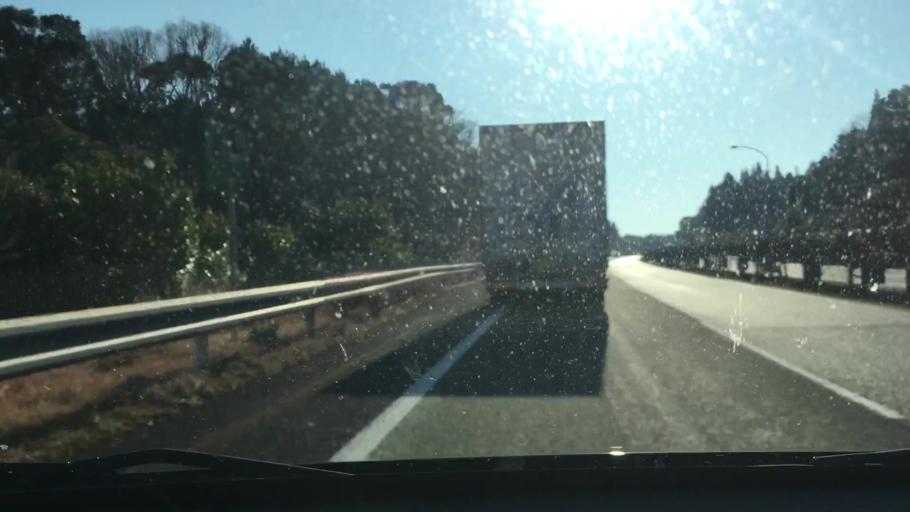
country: JP
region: Kagoshima
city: Kajiki
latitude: 31.8971
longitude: 130.7046
